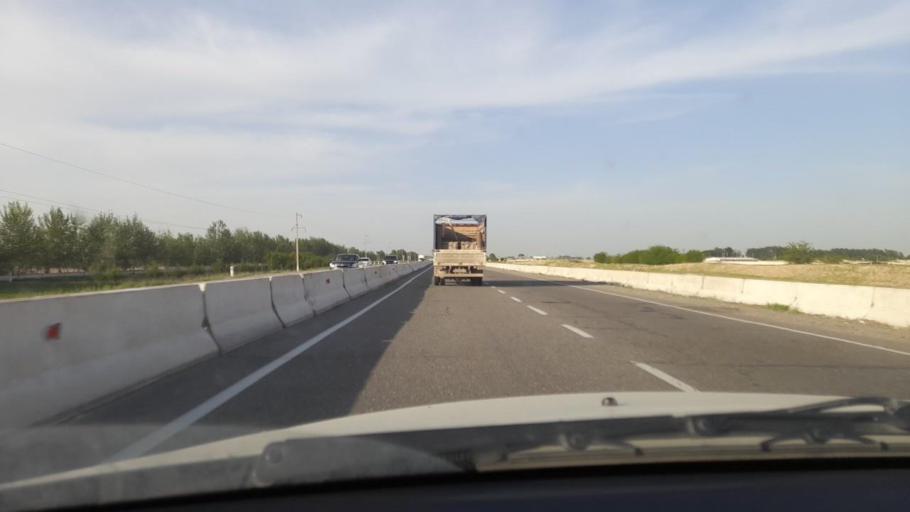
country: UZ
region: Jizzax
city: Paxtakor
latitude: 40.3017
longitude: 68.0734
